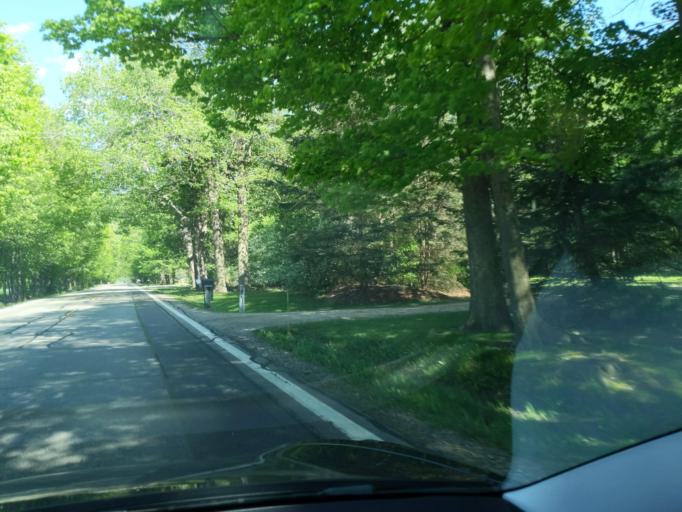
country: US
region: Michigan
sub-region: Barry County
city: Middleville
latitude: 42.7983
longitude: -85.3618
